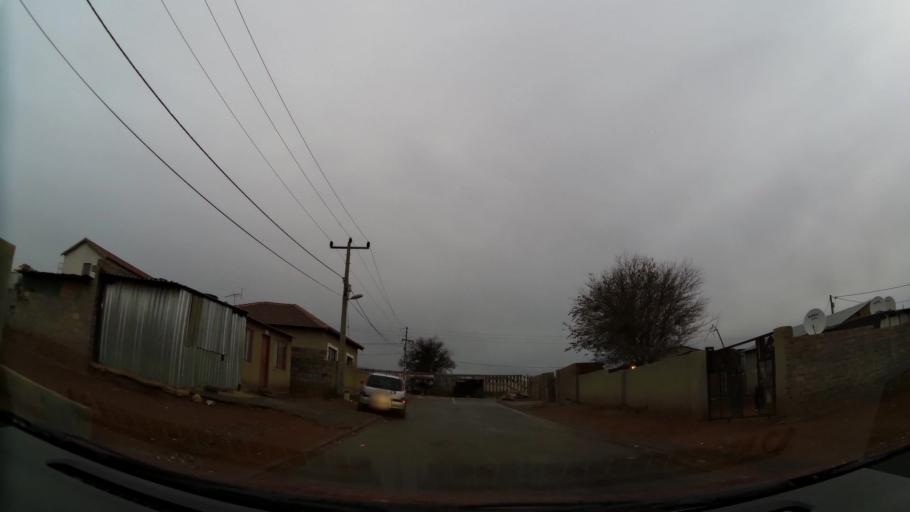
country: ZA
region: Gauteng
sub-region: City of Johannesburg Metropolitan Municipality
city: Roodepoort
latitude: -26.1736
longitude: 27.7893
